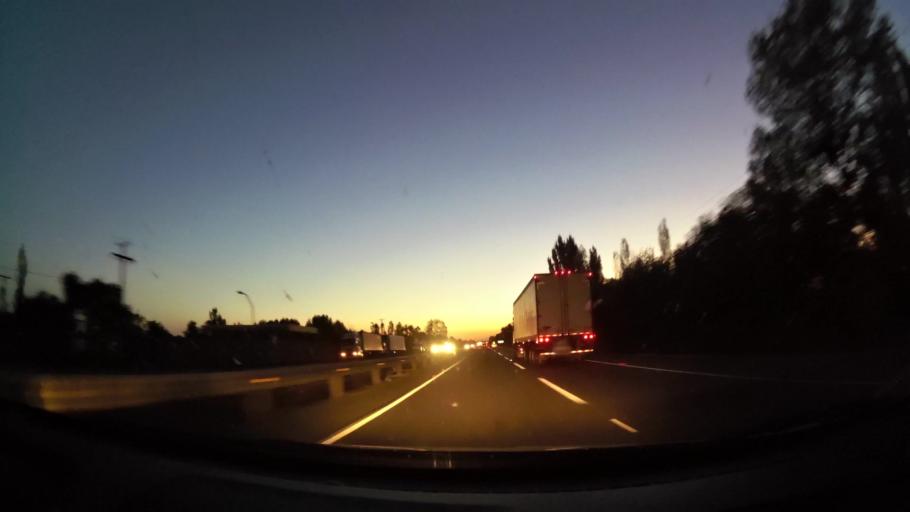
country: CL
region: Biobio
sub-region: Provincia de Nuble
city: San Carlos
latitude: -36.3563
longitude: -71.8699
